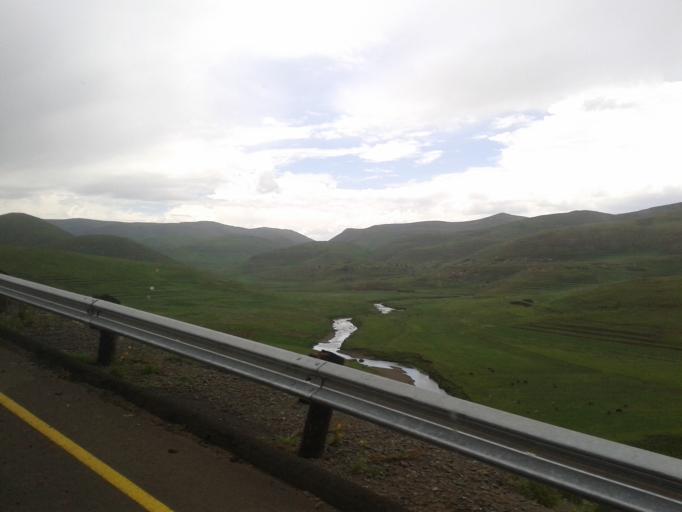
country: LS
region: Maseru
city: Nako
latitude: -29.7849
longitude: 28.0231
